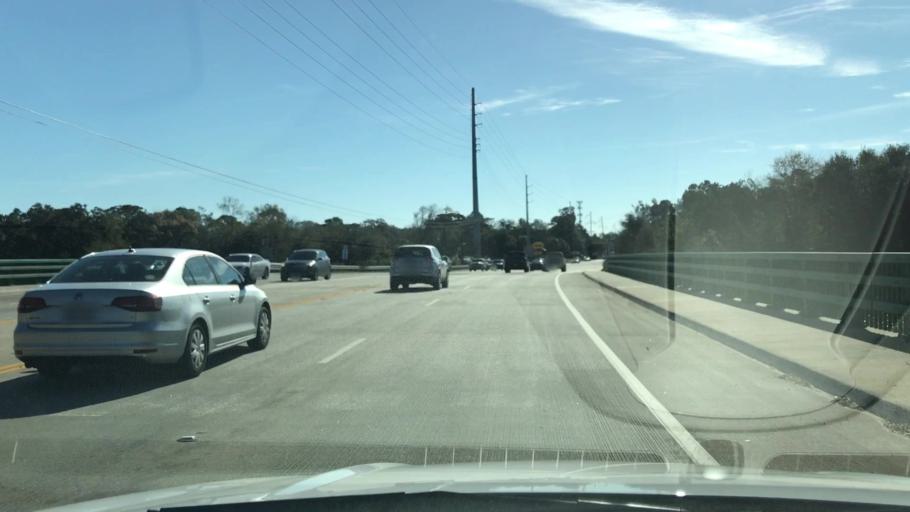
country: US
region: South Carolina
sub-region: Charleston County
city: Charleston
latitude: 32.7452
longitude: -79.9698
